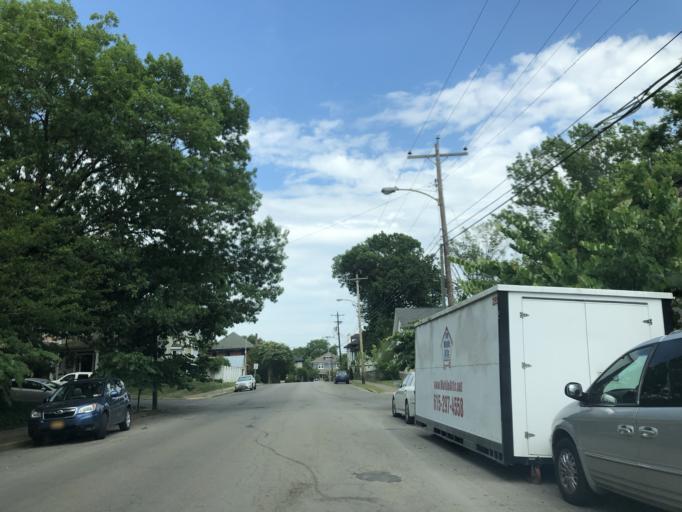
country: US
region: Tennessee
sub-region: Davidson County
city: Oak Hill
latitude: 36.1250
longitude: -86.7963
